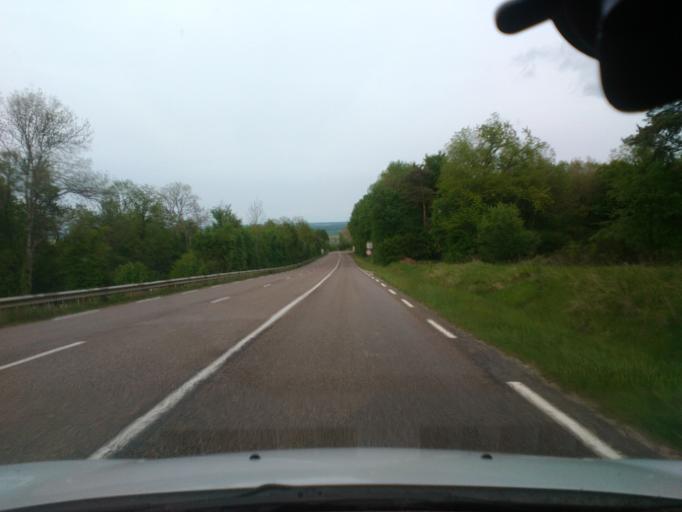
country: FR
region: Champagne-Ardenne
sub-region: Departement de la Haute-Marne
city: Chaumont
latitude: 48.1408
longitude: 5.0446
